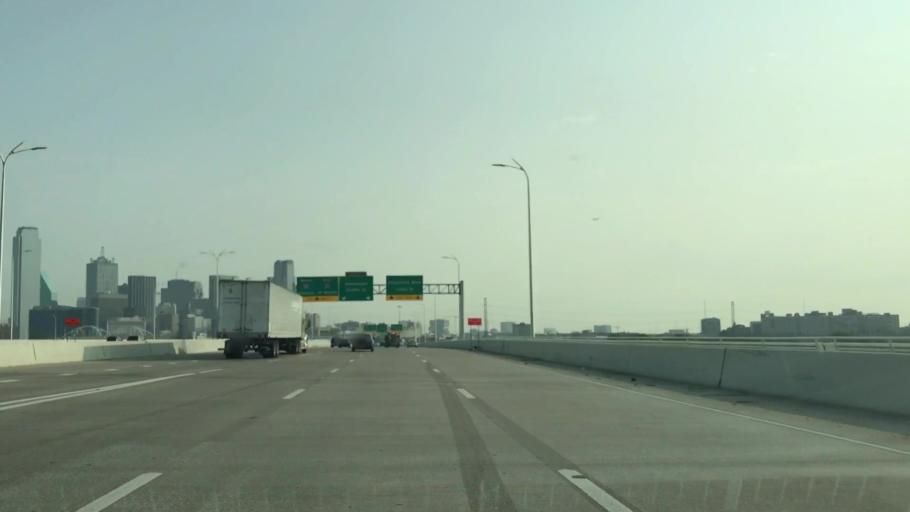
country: US
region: Texas
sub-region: Dallas County
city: Dallas
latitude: 32.7602
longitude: -96.8078
